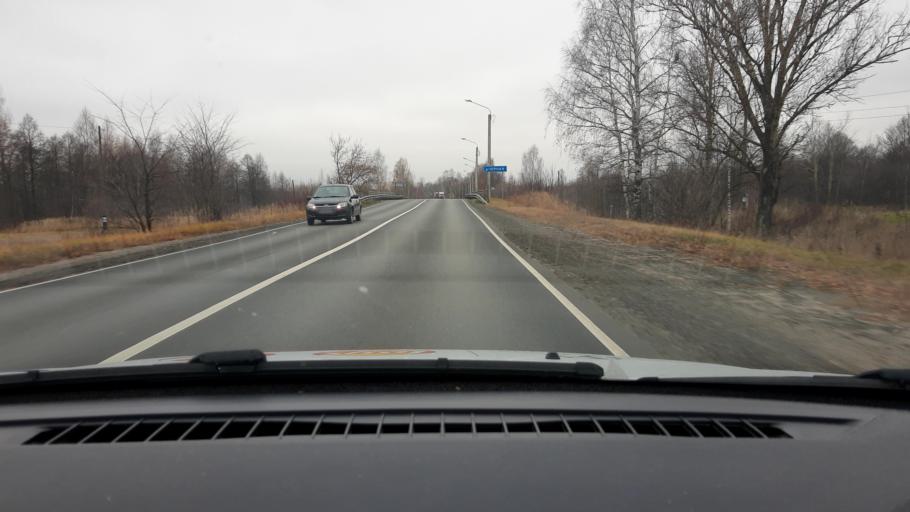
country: RU
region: Nizjnij Novgorod
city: Gorodets
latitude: 56.5929
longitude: 43.4622
